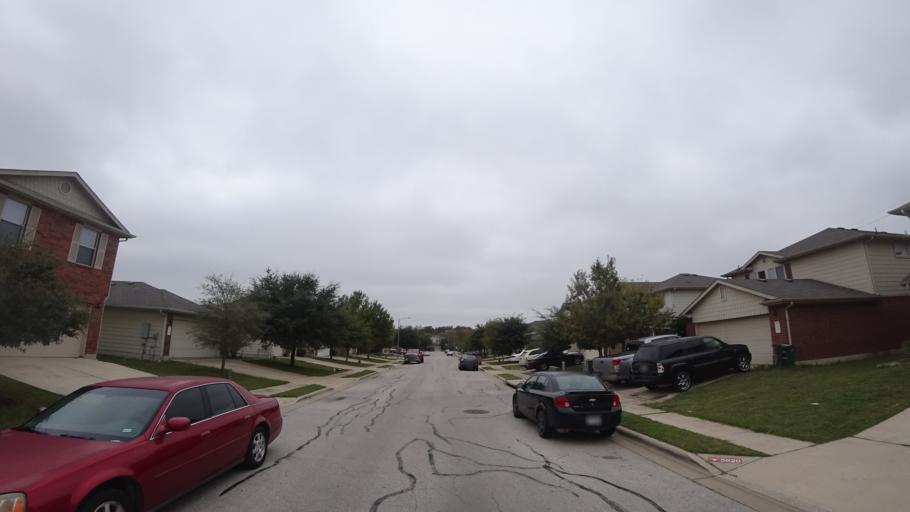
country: US
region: Texas
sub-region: Travis County
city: Manor
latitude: 30.3733
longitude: -97.6134
